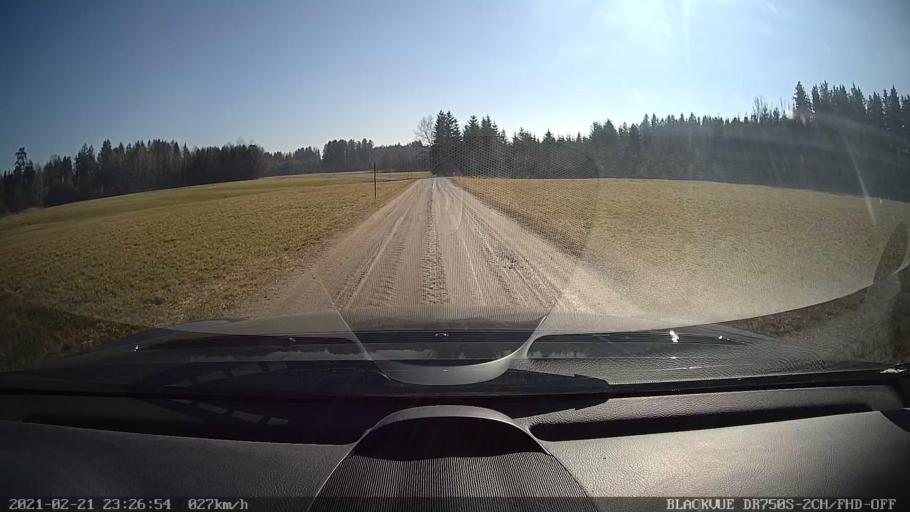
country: DE
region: Bavaria
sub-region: Upper Bavaria
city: Schonstett
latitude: 47.9991
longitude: 12.2265
